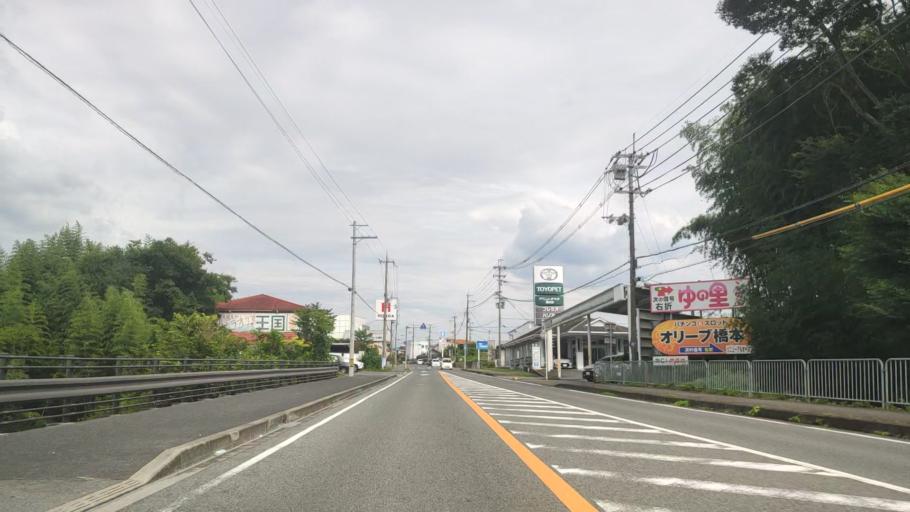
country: JP
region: Wakayama
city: Hashimoto
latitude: 34.3105
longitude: 135.5802
